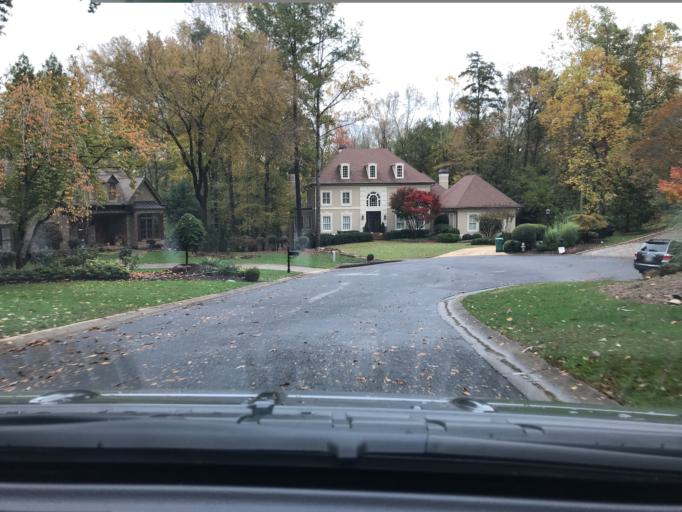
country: US
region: Georgia
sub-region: Fulton County
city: Johns Creek
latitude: 34.0069
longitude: -84.2294
